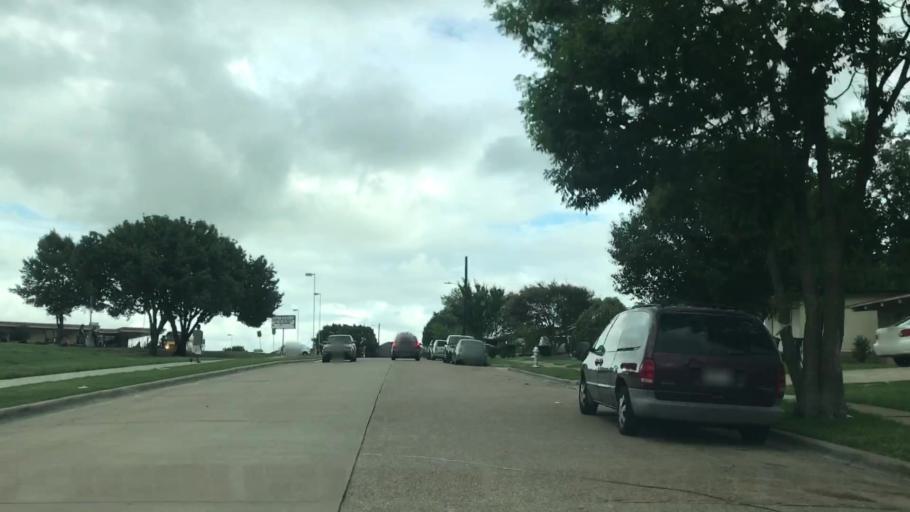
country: US
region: Texas
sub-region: Dallas County
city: Garland
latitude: 32.8972
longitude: -96.6173
